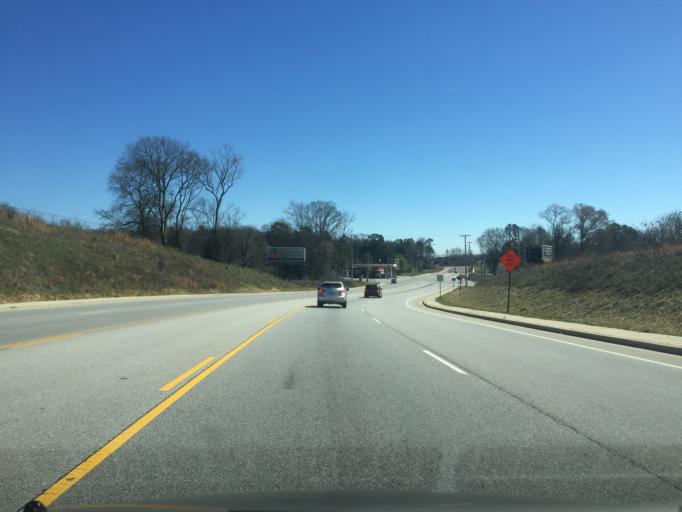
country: US
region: Tennessee
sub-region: Hamilton County
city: Collegedale
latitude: 35.0703
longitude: -85.1028
